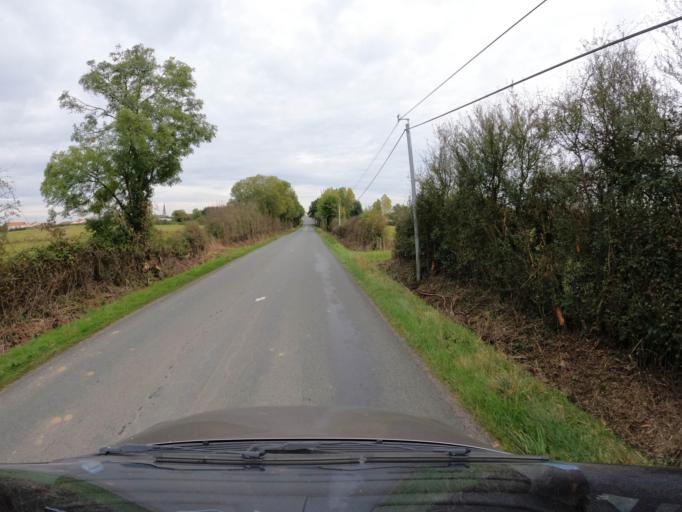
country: FR
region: Pays de la Loire
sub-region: Departement de Maine-et-Loire
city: Saint-Christophe-du-Bois
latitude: 47.0262
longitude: -0.9528
